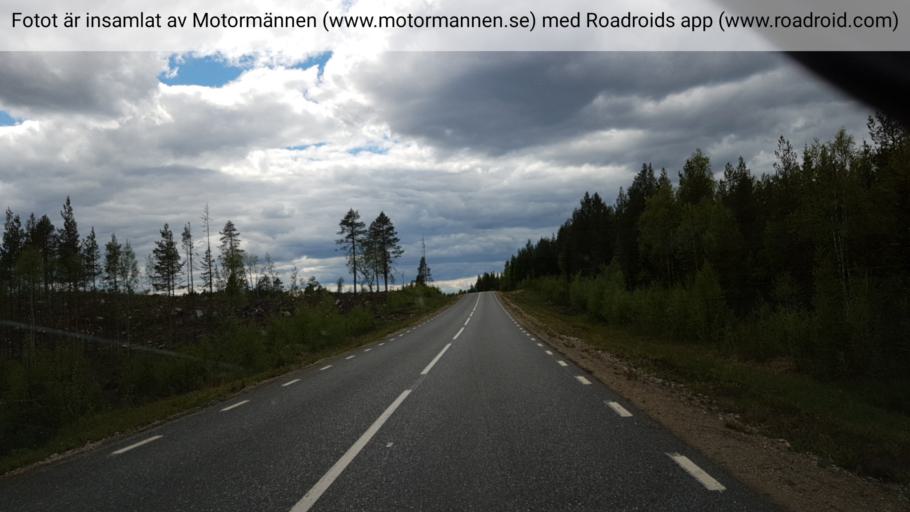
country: SE
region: Vaesterbotten
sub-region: Vindelns Kommun
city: Vindeln
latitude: 64.5385
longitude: 19.9030
